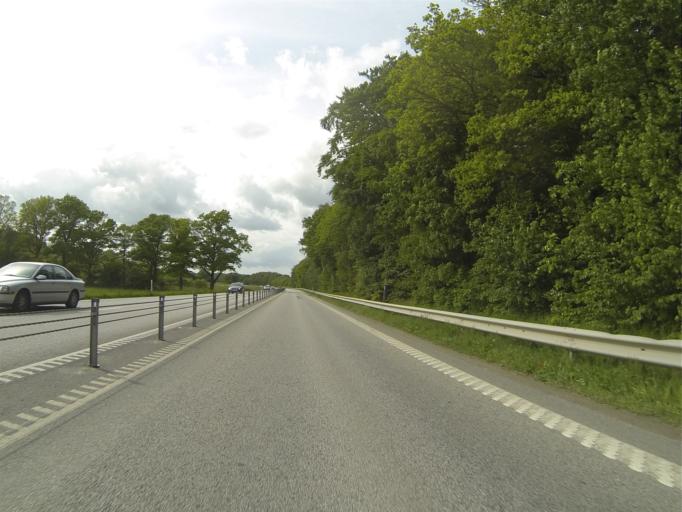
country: SE
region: Skane
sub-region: Lunds Kommun
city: Veberod
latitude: 55.6504
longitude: 13.4505
